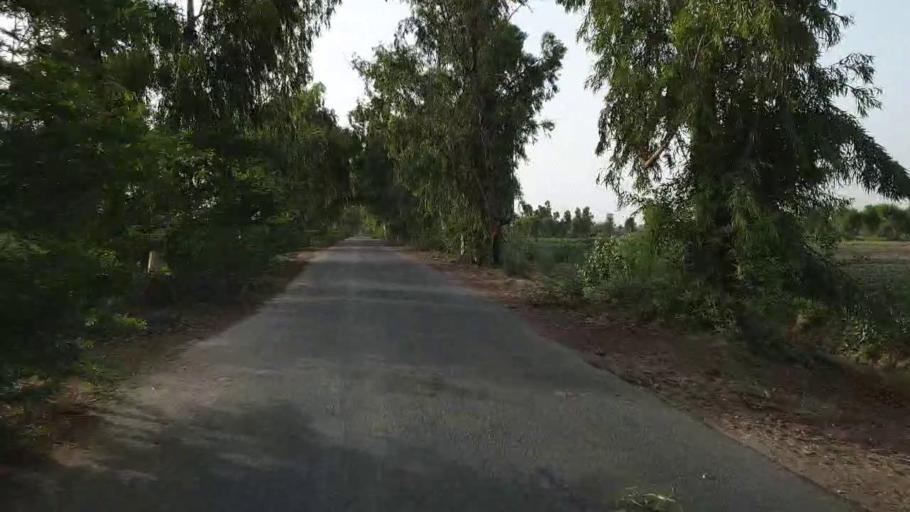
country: PK
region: Sindh
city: Bozdar
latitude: 27.1149
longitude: 68.9580
